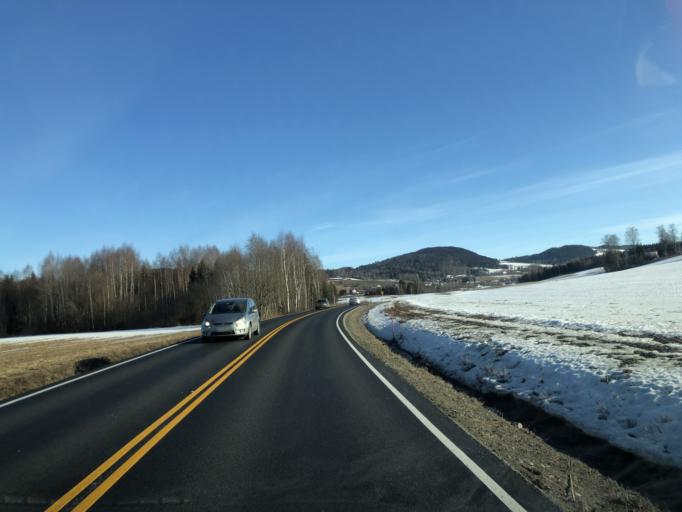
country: NO
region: Hedmark
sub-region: Ringsaker
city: Moelv
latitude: 60.9038
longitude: 10.7324
